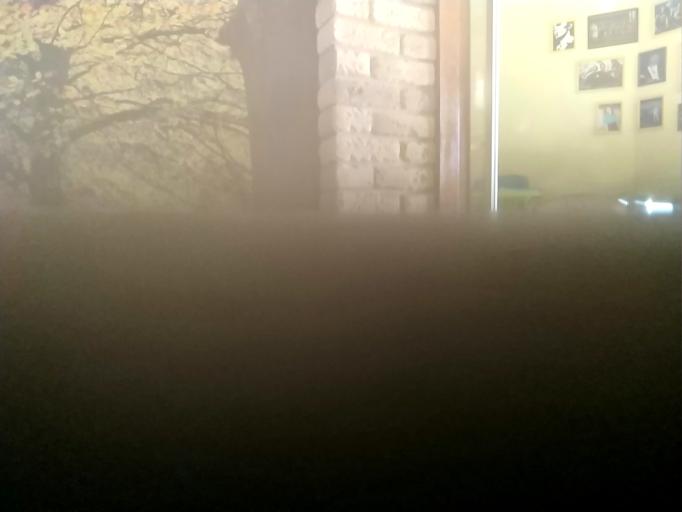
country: RU
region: Kaluga
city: Yukhnov
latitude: 54.8179
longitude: 35.0068
